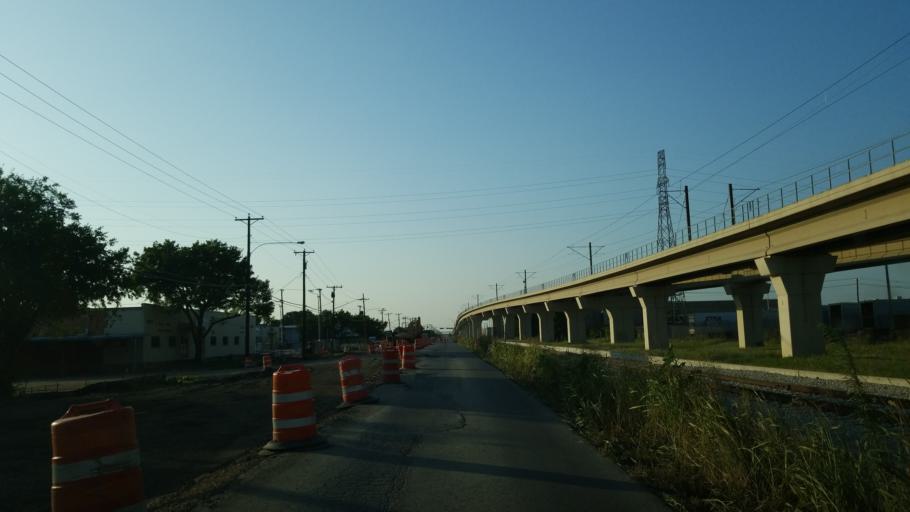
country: US
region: Texas
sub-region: Dallas County
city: Farmers Branch
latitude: 32.8833
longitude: -96.8845
